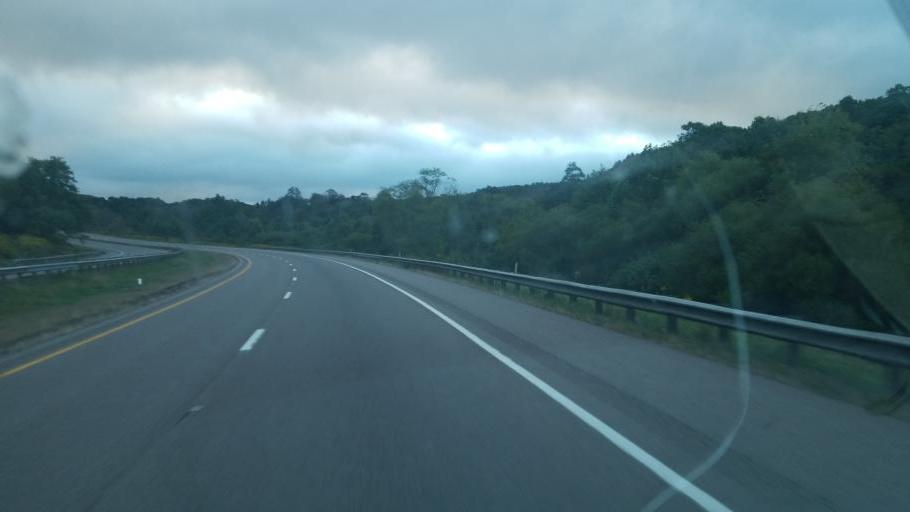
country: US
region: Maryland
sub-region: Garrett County
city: Oakland
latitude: 39.6972
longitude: -79.3228
